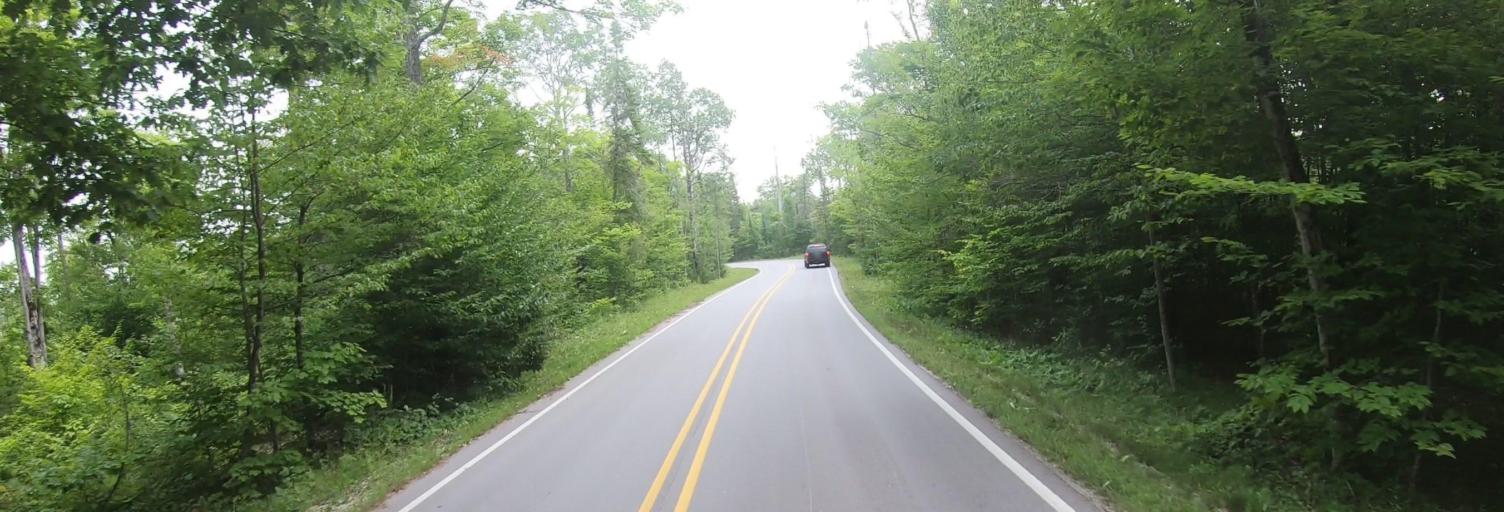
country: CA
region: Ontario
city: Thessalon
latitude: 45.9432
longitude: -83.5814
